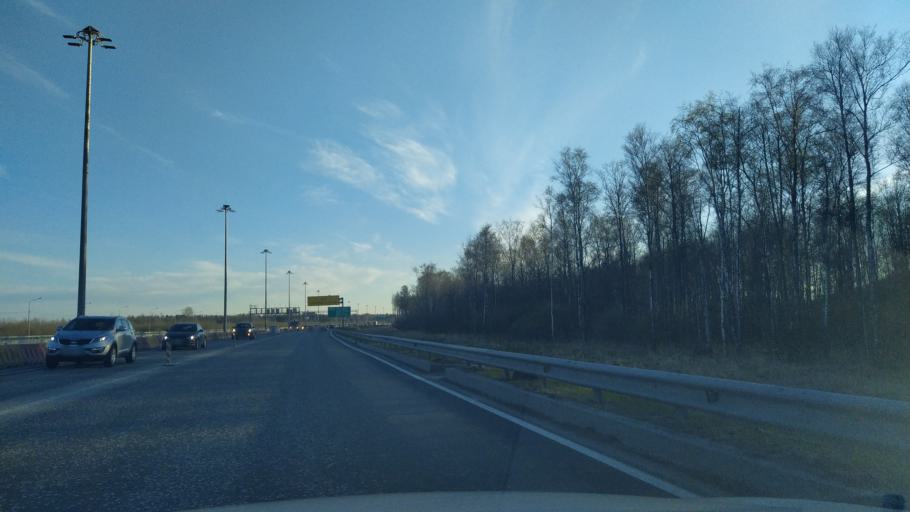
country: RU
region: St.-Petersburg
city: Levashovo
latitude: 60.0688
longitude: 30.1721
